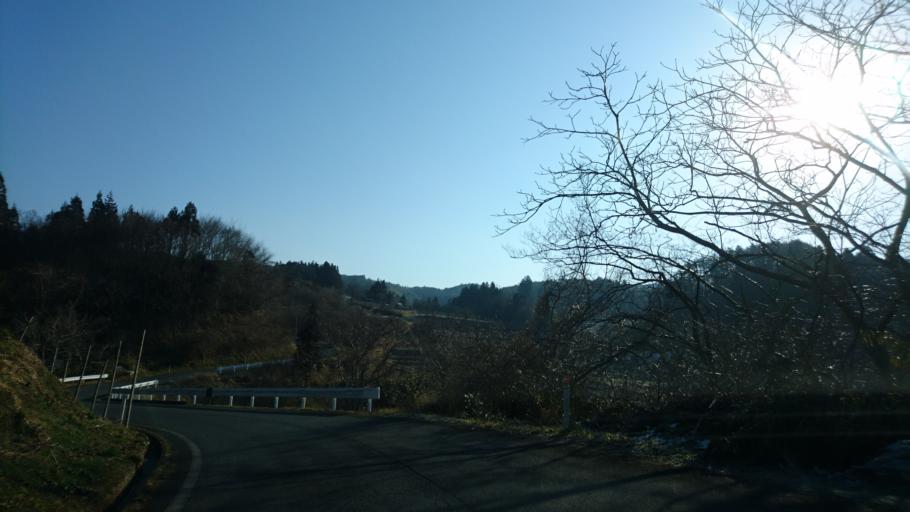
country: JP
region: Iwate
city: Ichinoseki
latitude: 38.9144
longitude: 141.2834
